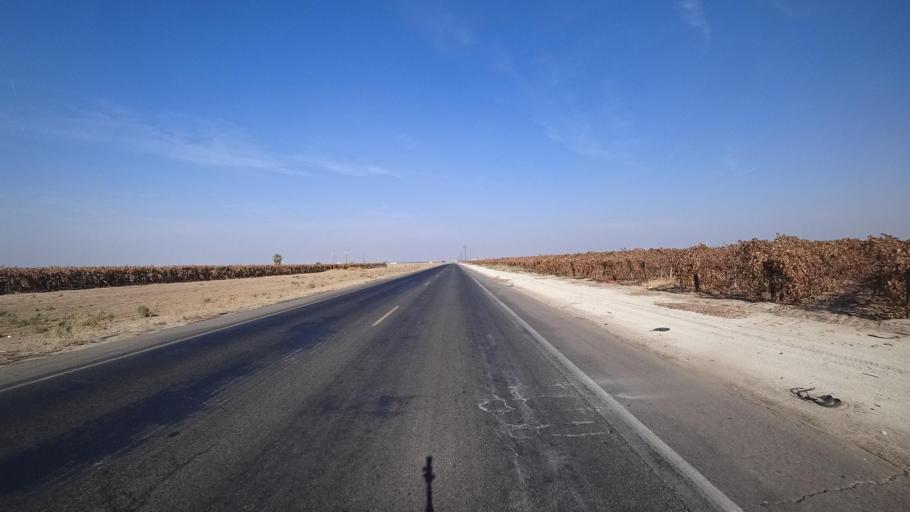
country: US
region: California
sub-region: Kern County
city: McFarland
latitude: 35.7087
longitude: -119.1654
